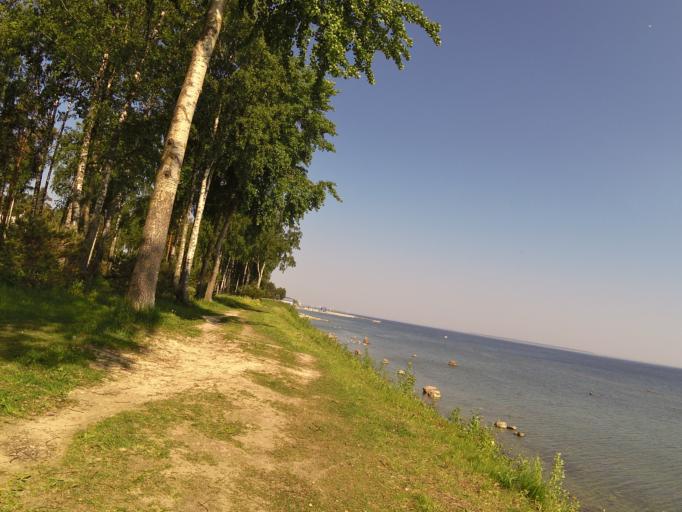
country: EE
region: Harju
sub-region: Harku vald
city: Tabasalu
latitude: 59.4440
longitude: 24.6215
